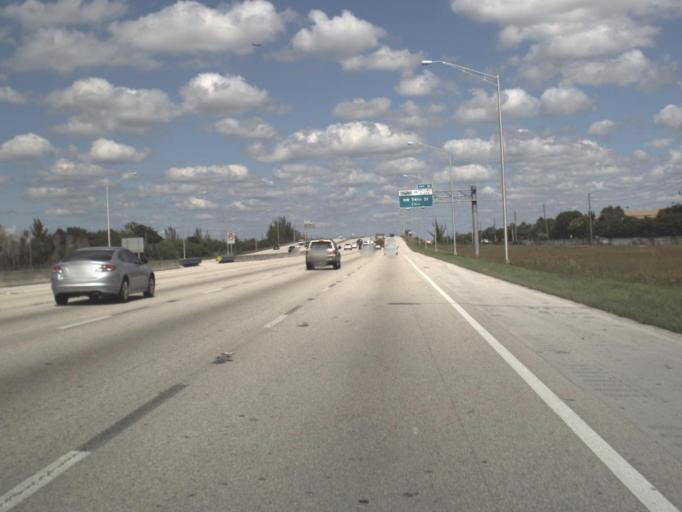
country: US
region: Florida
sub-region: Miami-Dade County
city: Doral
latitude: 25.8207
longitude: -80.3865
